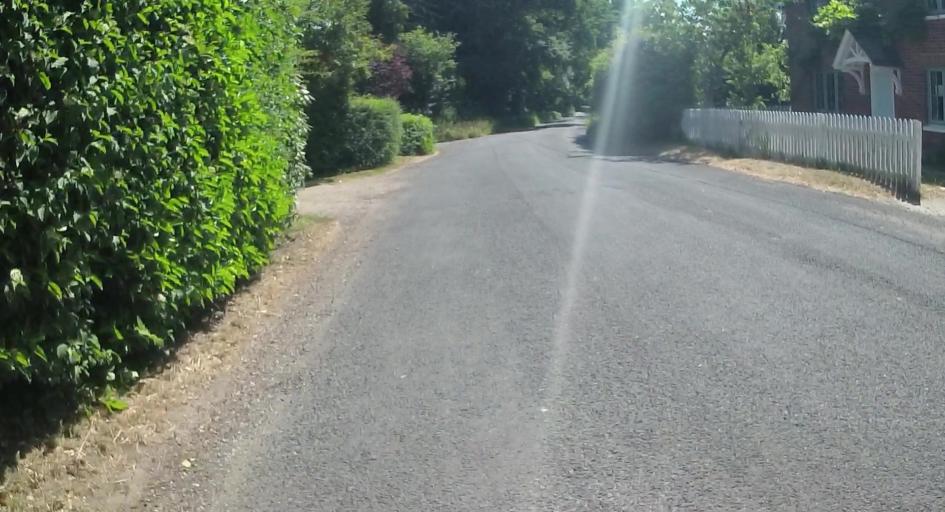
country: GB
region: England
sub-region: Hampshire
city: Kingsclere
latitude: 51.3418
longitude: -1.2795
